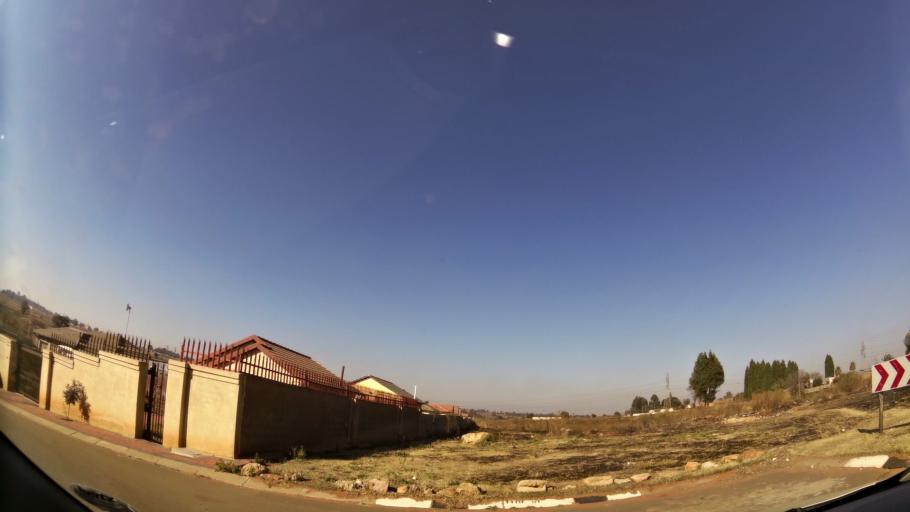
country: ZA
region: Gauteng
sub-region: City of Johannesburg Metropolitan Municipality
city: Roodepoort
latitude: -26.1632
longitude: 27.8336
